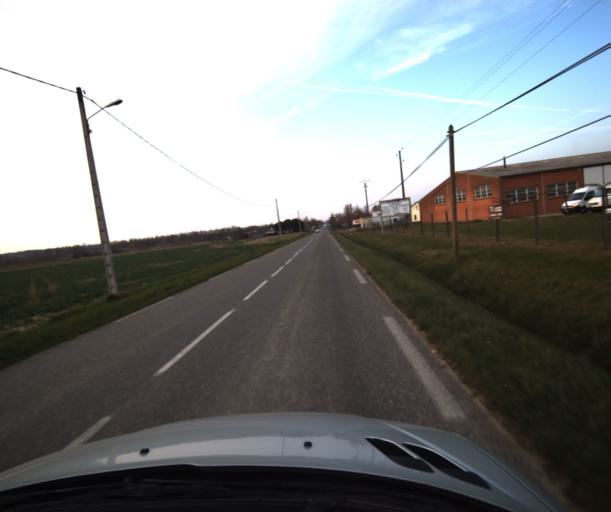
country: FR
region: Midi-Pyrenees
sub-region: Departement de la Haute-Garonne
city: Fronton
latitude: 43.8493
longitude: 1.3871
